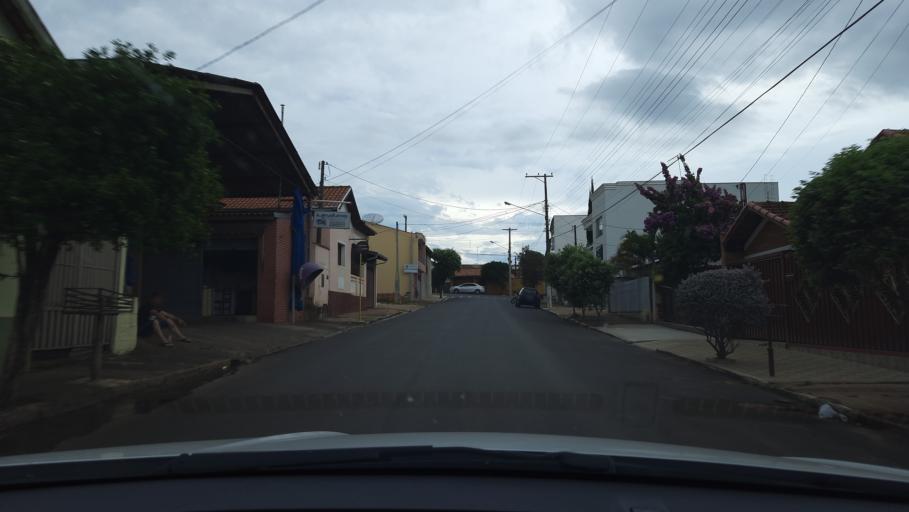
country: BR
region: Sao Paulo
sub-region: Casa Branca
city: Casa Branca
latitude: -21.7802
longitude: -47.0803
